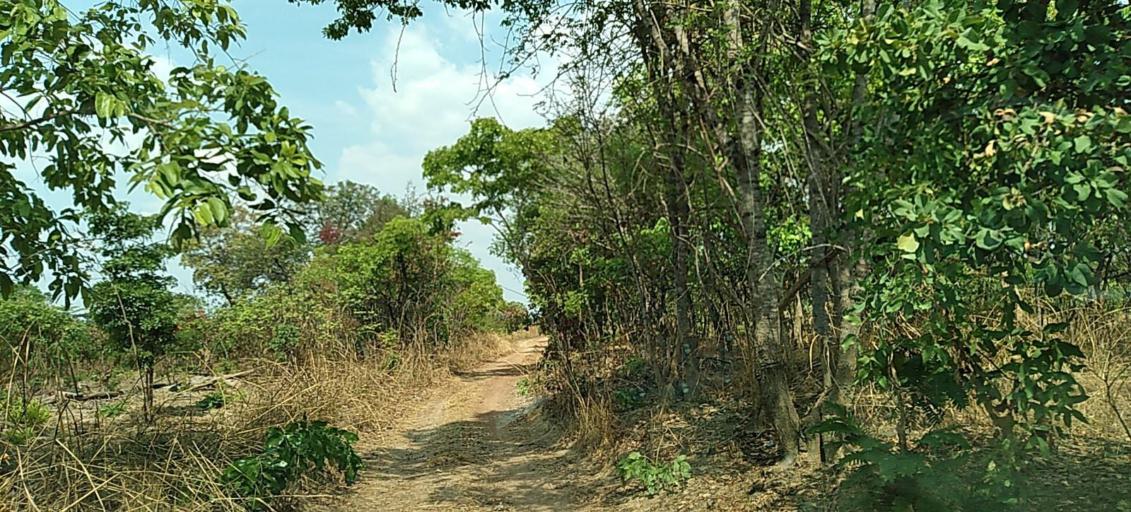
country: ZM
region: Copperbelt
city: Chililabombwe
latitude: -12.3405
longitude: 27.7838
